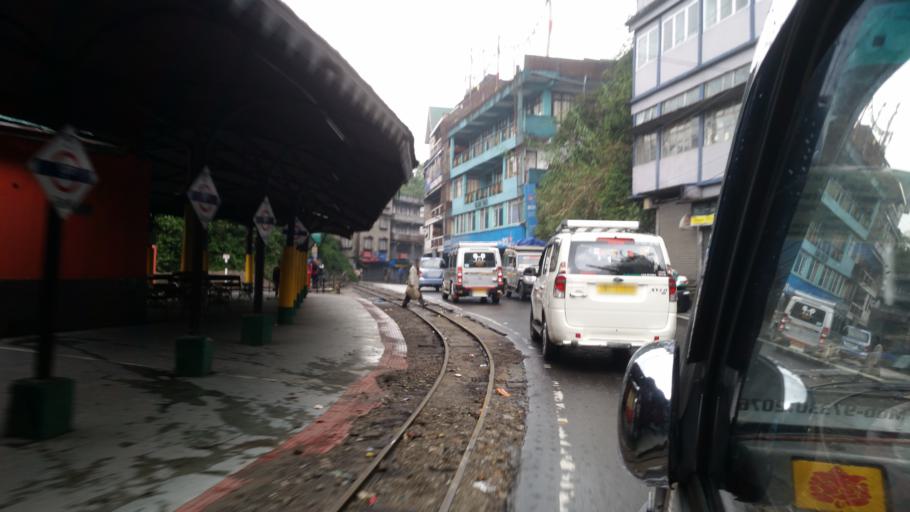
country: IN
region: West Bengal
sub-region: Darjiling
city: Darjiling
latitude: 27.0084
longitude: 88.2537
